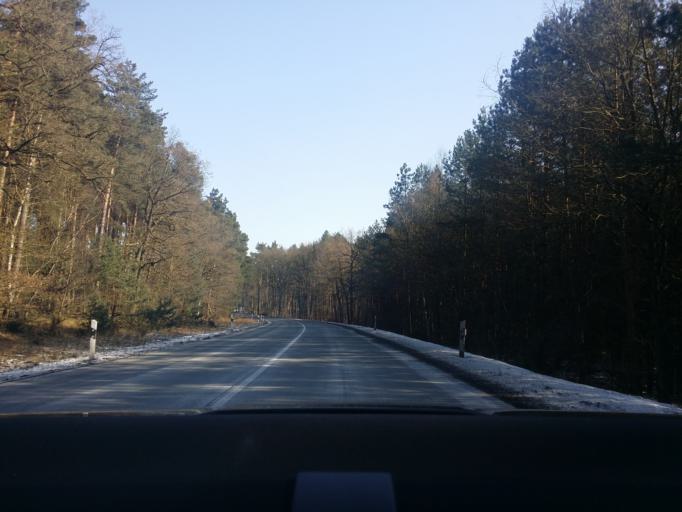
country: DE
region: Brandenburg
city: Perleberg
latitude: 53.0922
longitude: 11.9215
